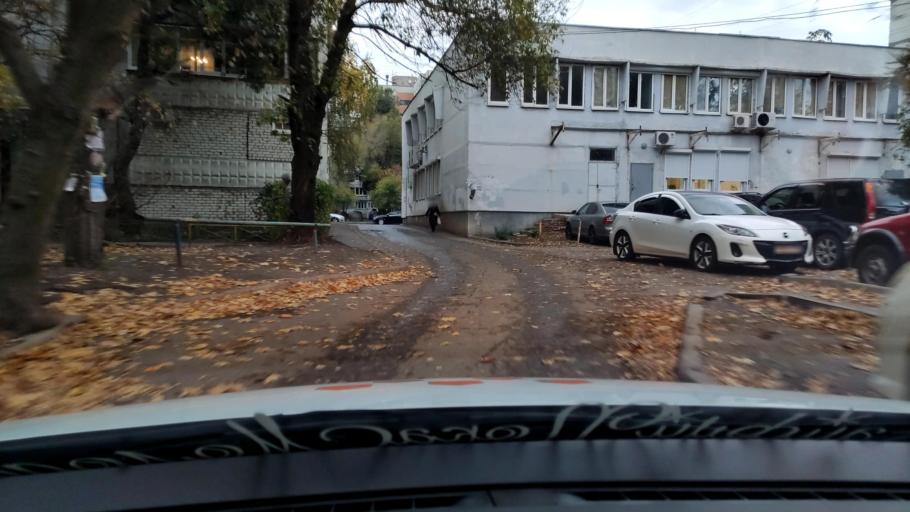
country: RU
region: Voronezj
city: Podgornoye
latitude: 51.7055
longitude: 39.1696
